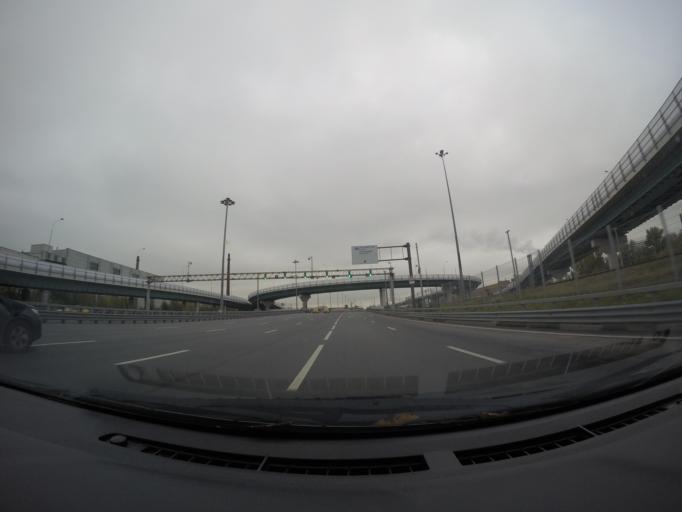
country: RU
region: Moscow
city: Ryazanskiy
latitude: 55.7622
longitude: 37.7473
